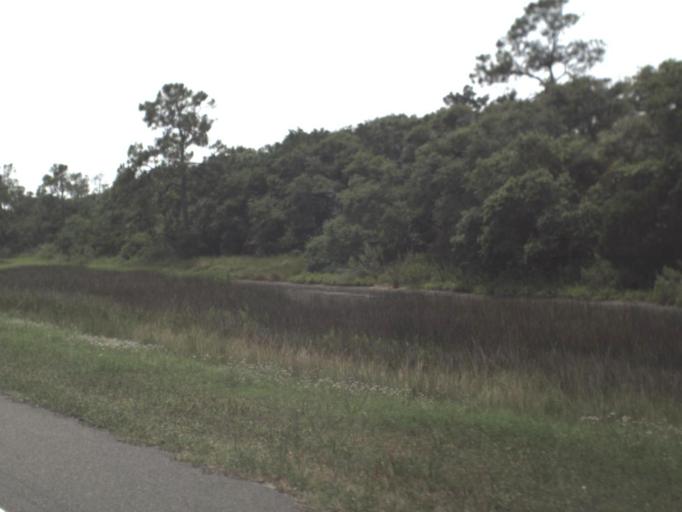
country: US
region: Florida
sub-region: Nassau County
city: Fernandina Beach
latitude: 30.5289
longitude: -81.4399
